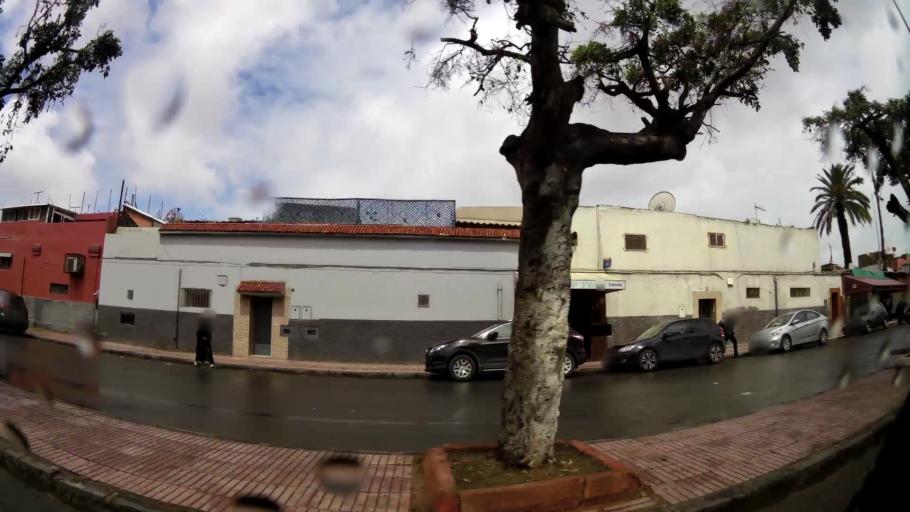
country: MA
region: Grand Casablanca
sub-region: Casablanca
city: Casablanca
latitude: 33.5752
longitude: -7.5953
